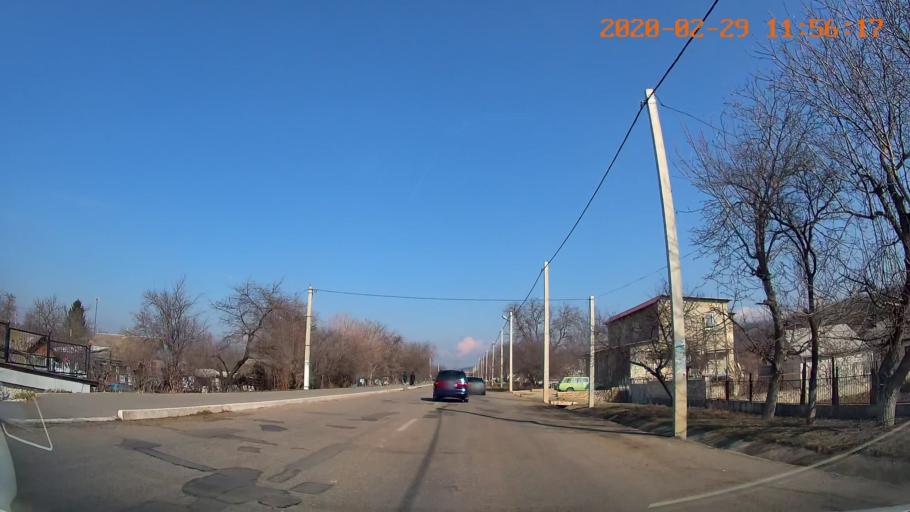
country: MD
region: Telenesti
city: Ribnita
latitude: 47.7953
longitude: 29.0012
